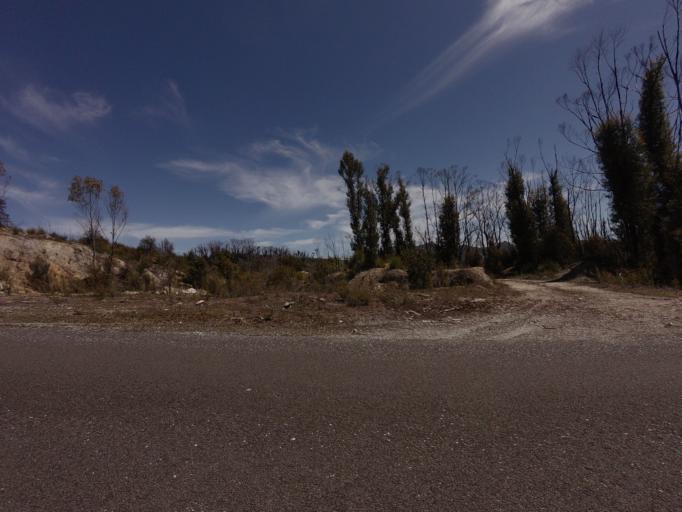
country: AU
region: Tasmania
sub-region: Huon Valley
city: Geeveston
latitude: -42.8511
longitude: 146.2352
